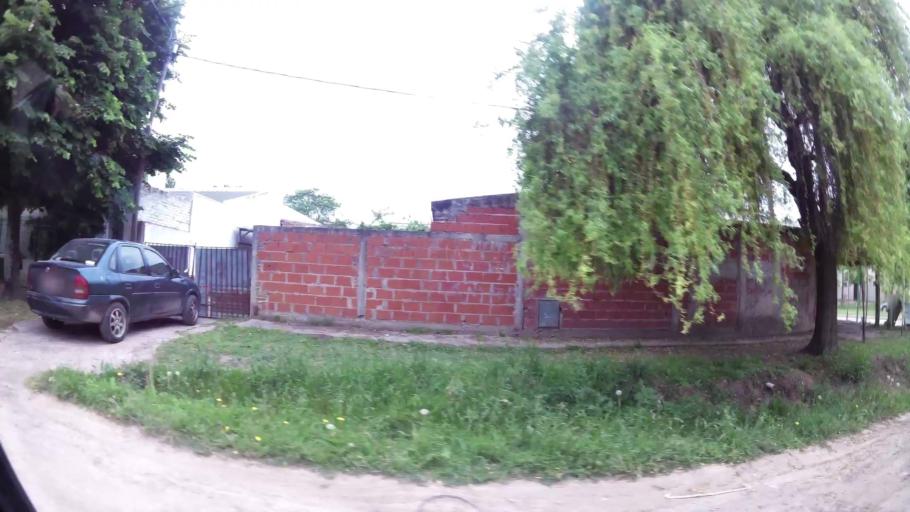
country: AR
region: Buenos Aires
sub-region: Partido de La Plata
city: La Plata
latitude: -34.9354
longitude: -58.0050
